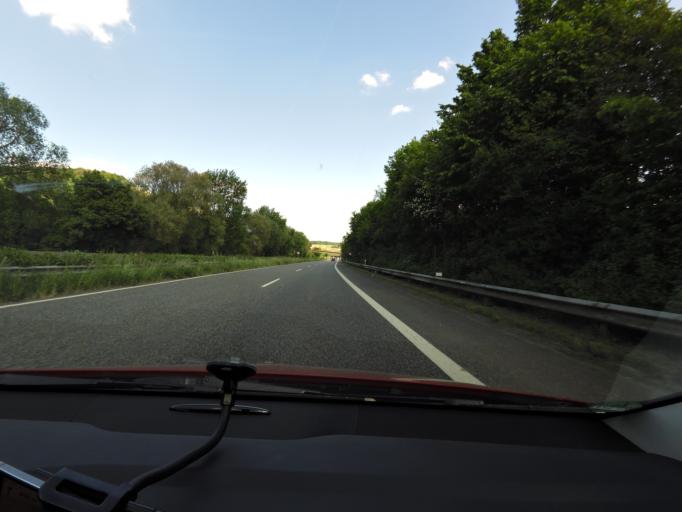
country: DE
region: Rheinland-Pfalz
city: Konigsfeld
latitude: 50.5470
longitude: 7.1720
